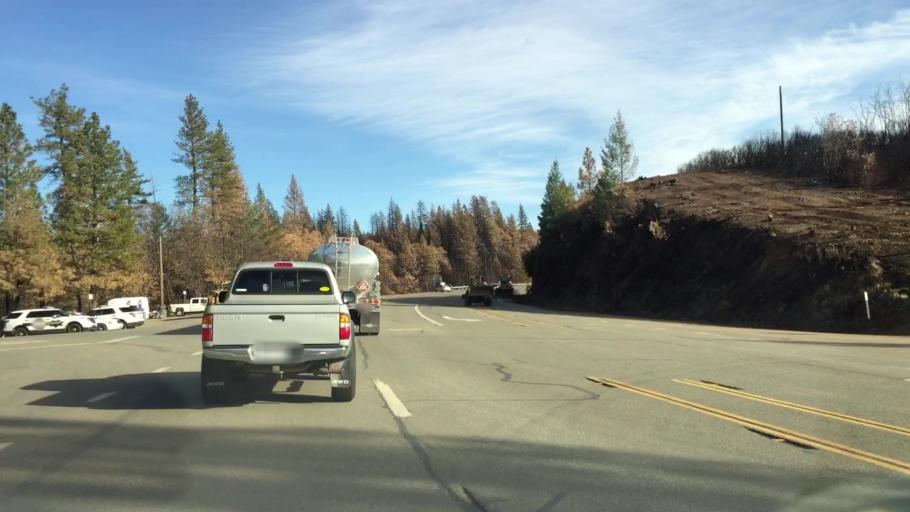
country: US
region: California
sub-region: Butte County
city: Paradise
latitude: 39.7160
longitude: -121.5213
